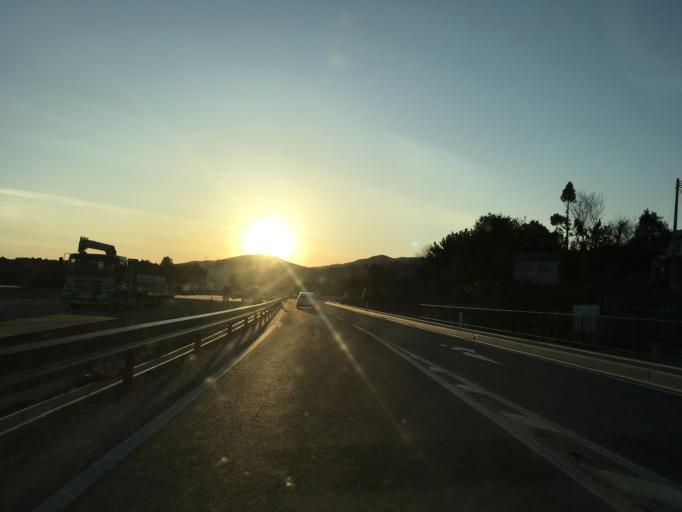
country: JP
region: Iwate
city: Ofunato
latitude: 38.8144
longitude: 141.5671
